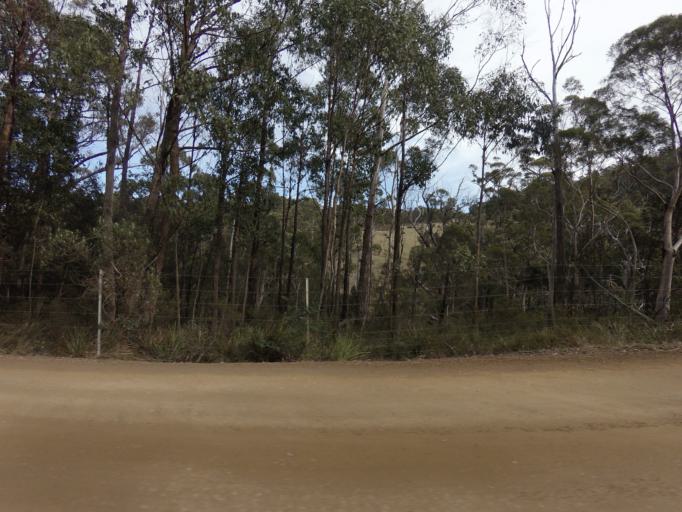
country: AU
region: Tasmania
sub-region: Huon Valley
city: Huonville
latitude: -43.0641
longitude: 147.0893
